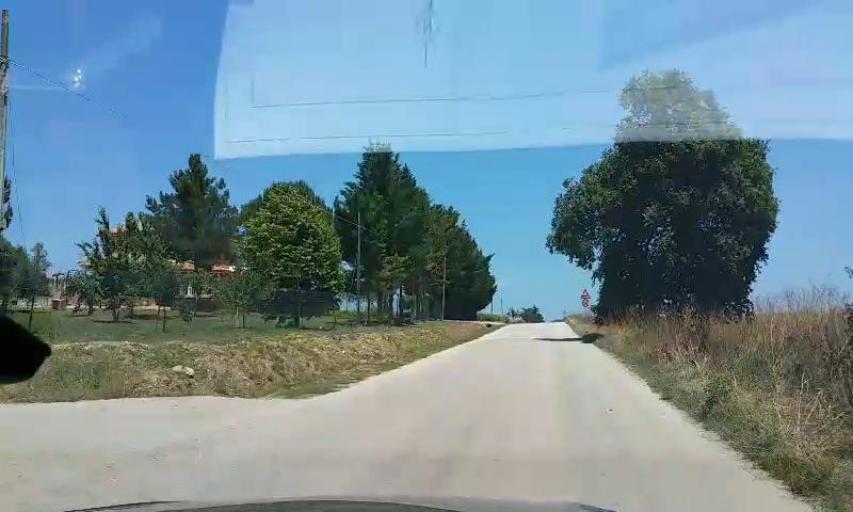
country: IT
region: Molise
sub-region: Provincia di Campobasso
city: San Giacomo degli Schiavoni
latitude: 41.9642
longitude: 14.9004
